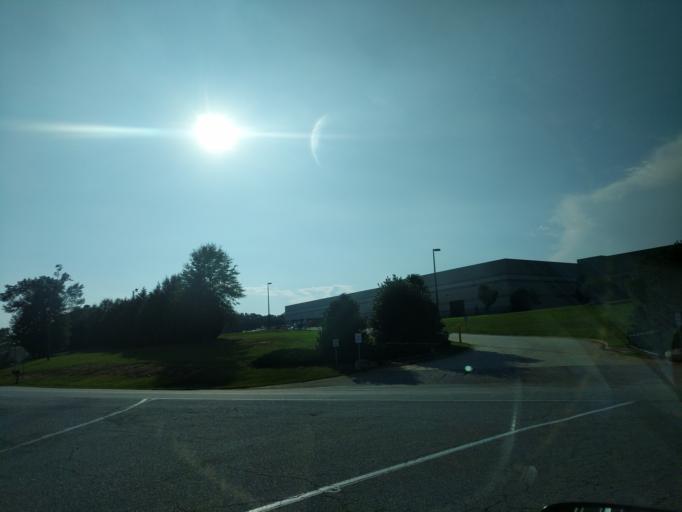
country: US
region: South Carolina
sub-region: Anderson County
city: Piedmont
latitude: 34.7082
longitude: -82.5033
